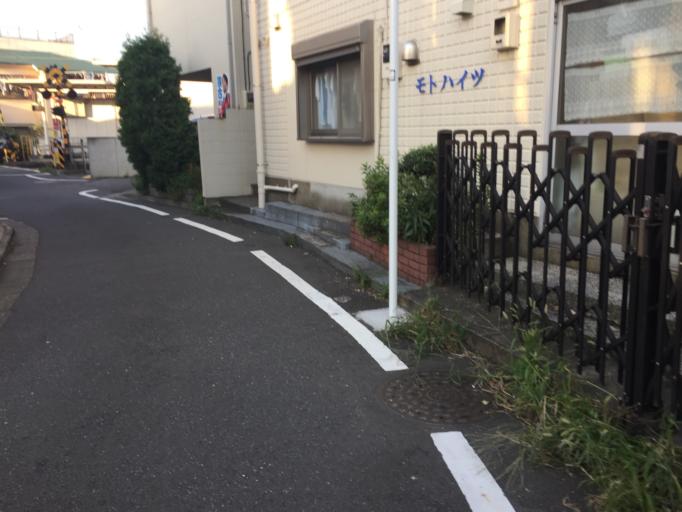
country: JP
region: Tokyo
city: Tokyo
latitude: 35.6445
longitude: 139.6660
